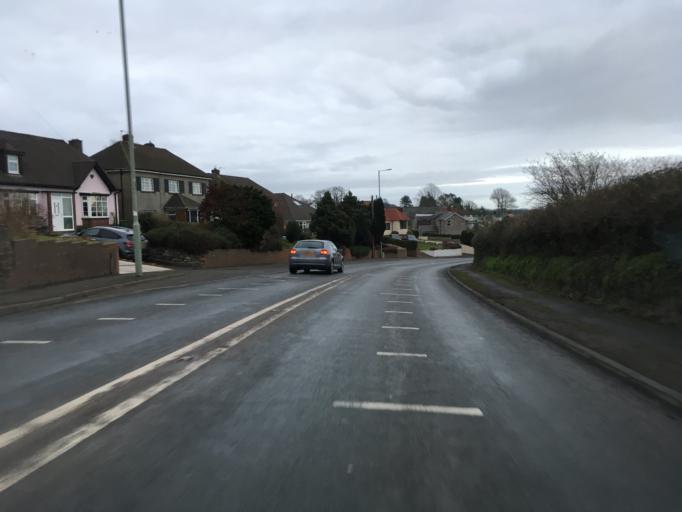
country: GB
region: Wales
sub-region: Rhondda Cynon Taf
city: Llantrisant
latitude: 51.5206
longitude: -3.3448
